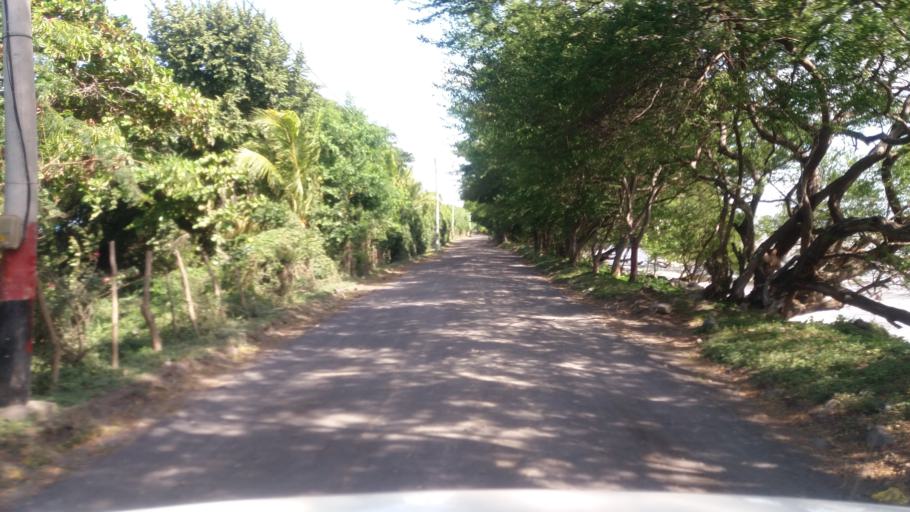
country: NI
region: Granada
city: Granada
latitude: 11.9879
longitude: -85.9390
